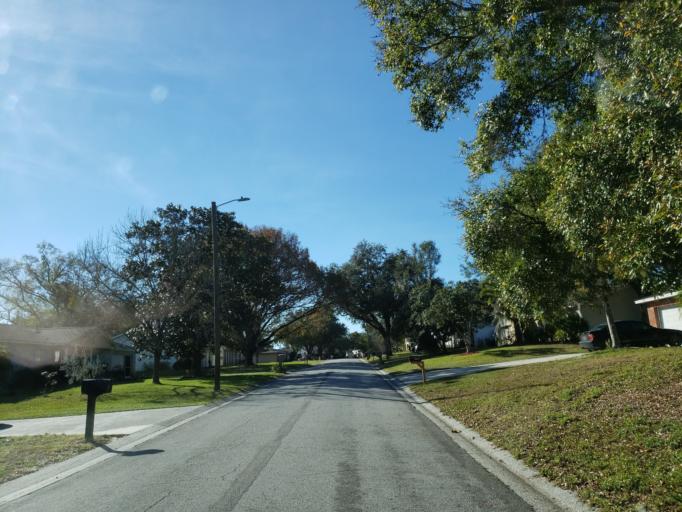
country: US
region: Florida
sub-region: Hillsborough County
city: Bloomingdale
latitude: 27.9034
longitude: -82.2709
